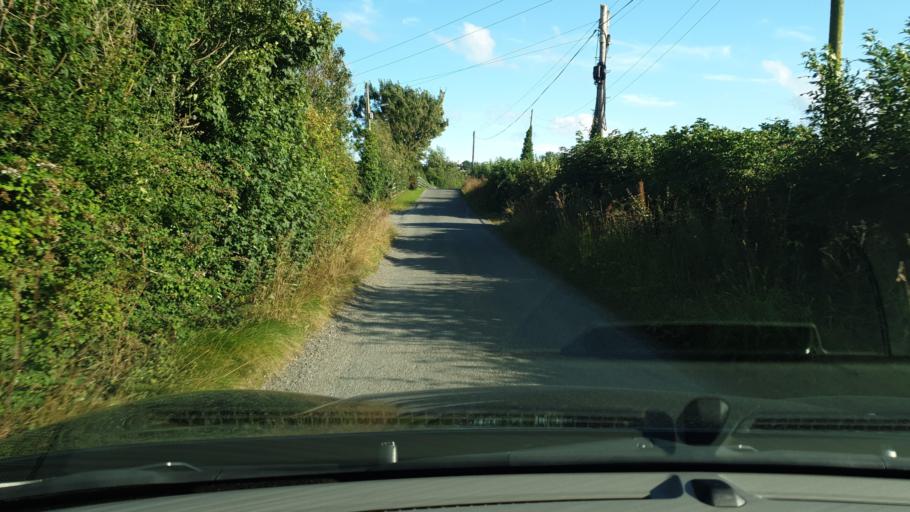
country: IE
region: Leinster
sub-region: An Mhi
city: Stamullin
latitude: 53.5815
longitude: -6.2455
